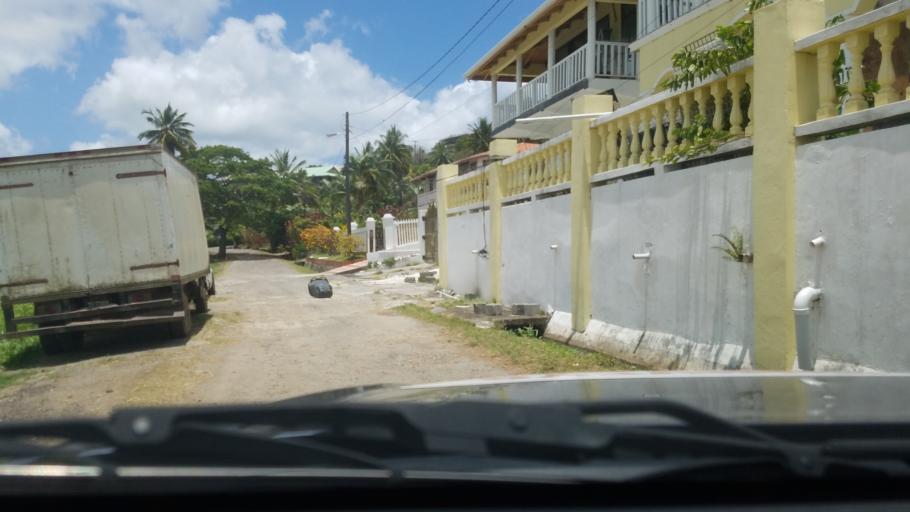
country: LC
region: Castries Quarter
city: Bisee
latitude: 14.0219
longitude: -60.9969
